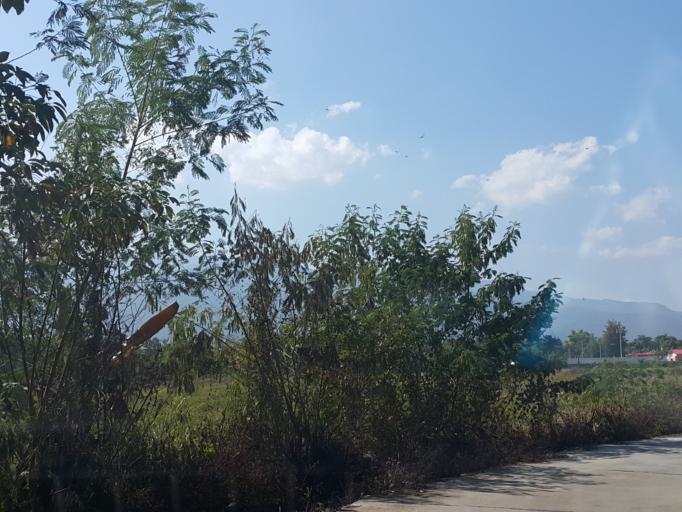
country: TH
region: Chiang Mai
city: San Sai
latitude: 18.8603
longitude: 98.9885
